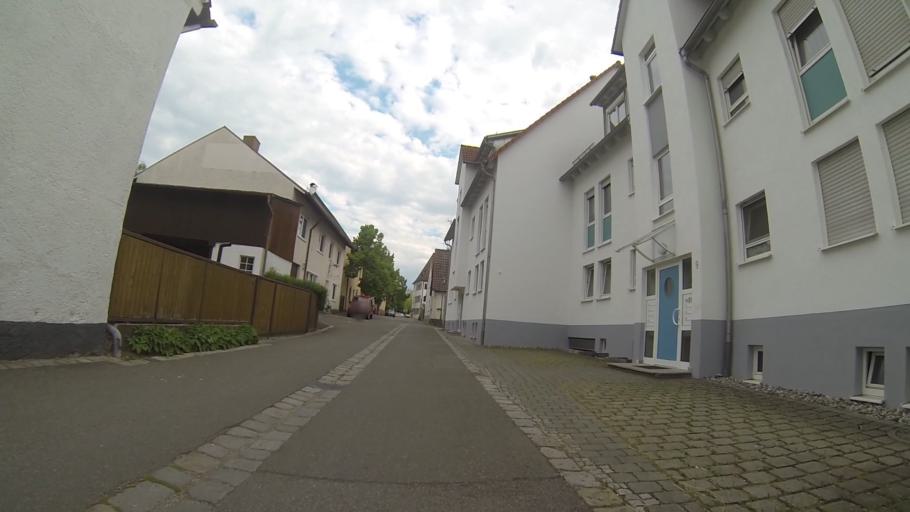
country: DE
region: Baden-Wuerttemberg
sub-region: Tuebingen Region
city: Langenau
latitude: 48.4973
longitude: 10.1179
